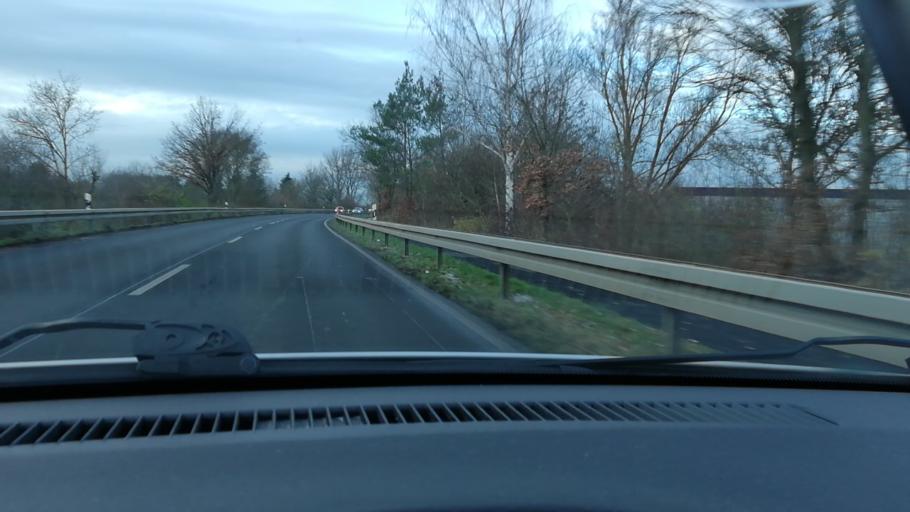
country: DE
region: Hesse
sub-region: Regierungsbezirk Darmstadt
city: Rodenbach
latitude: 50.1444
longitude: 9.0043
